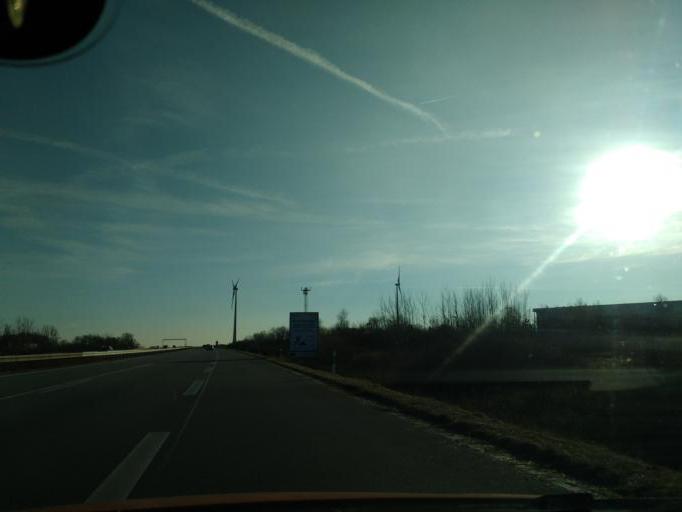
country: DE
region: Berlin
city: Buchholz
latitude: 52.6388
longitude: 13.4342
